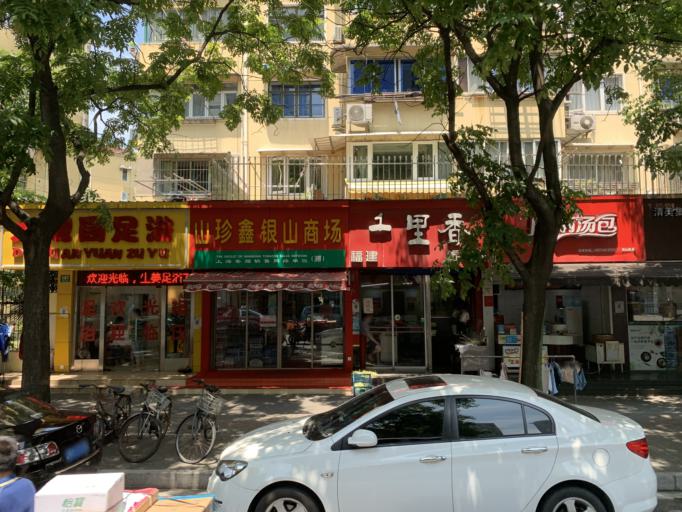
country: CN
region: Shanghai Shi
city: Huamu
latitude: 31.2482
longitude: 121.5799
